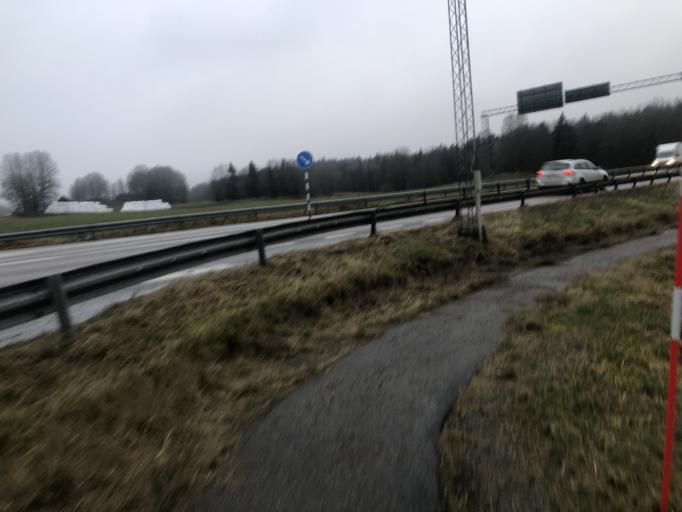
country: SE
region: Vaestra Goetaland
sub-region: Ulricehamns Kommun
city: Ulricehamn
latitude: 57.7971
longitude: 13.5381
